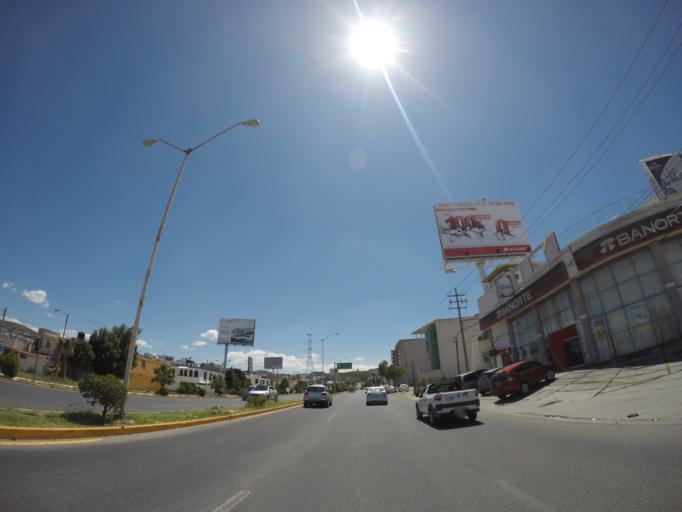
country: MX
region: San Luis Potosi
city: Escalerillas
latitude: 22.1337
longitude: -101.0313
